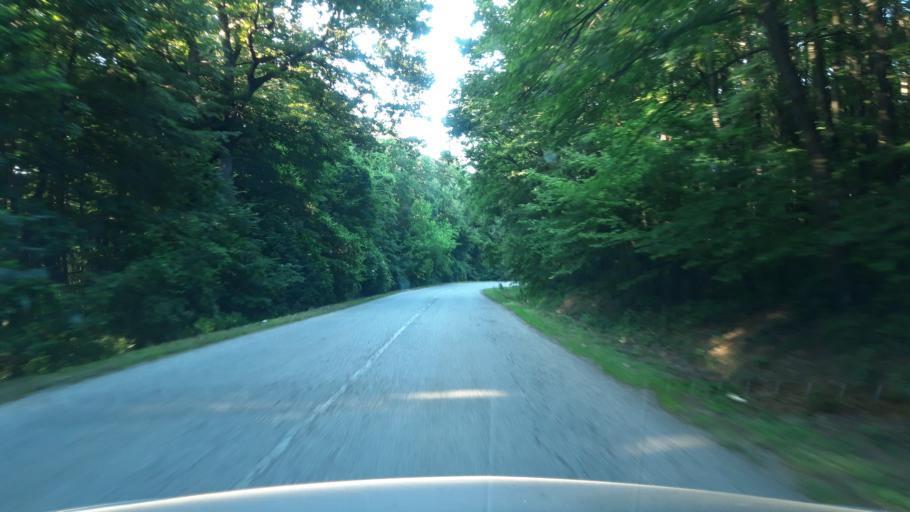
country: RS
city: Glozan
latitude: 45.1495
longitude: 19.5800
